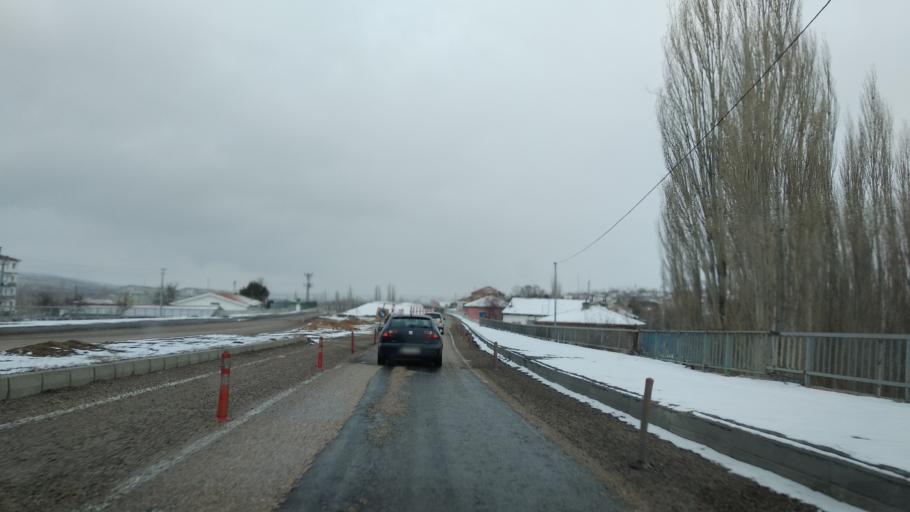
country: TR
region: Kayseri
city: Pinarbasi
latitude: 38.7265
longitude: 36.3973
